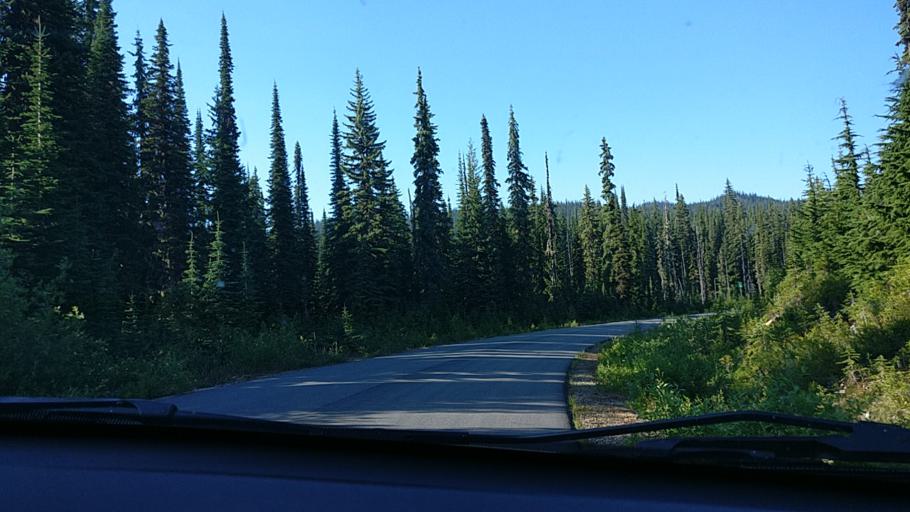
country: CA
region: British Columbia
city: Revelstoke
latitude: 51.0228
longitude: -118.1563
